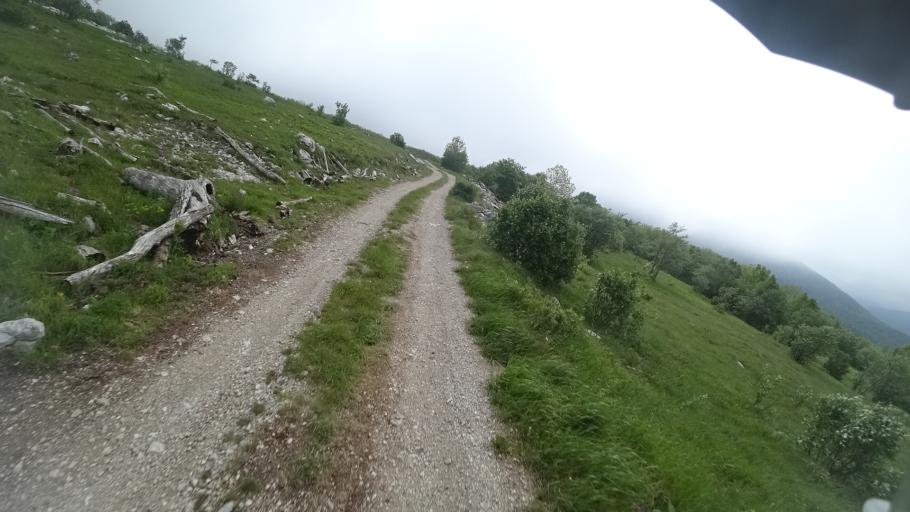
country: BA
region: Federation of Bosnia and Herzegovina
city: Bihac
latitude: 44.7019
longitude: 15.8246
